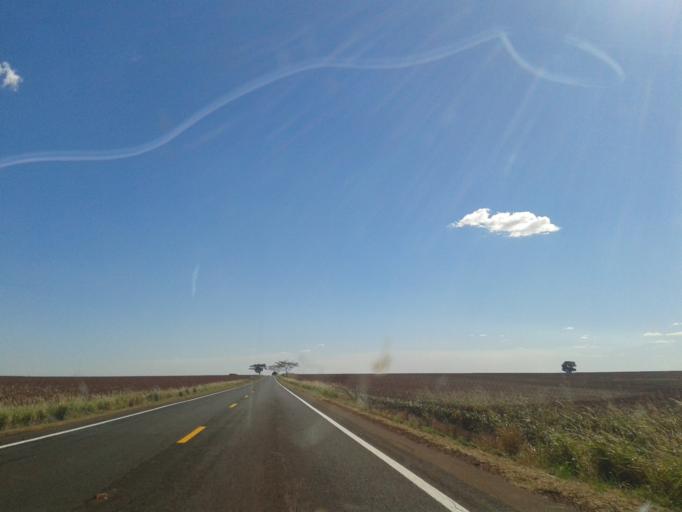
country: BR
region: Minas Gerais
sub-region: Capinopolis
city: Capinopolis
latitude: -18.6860
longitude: -49.5256
